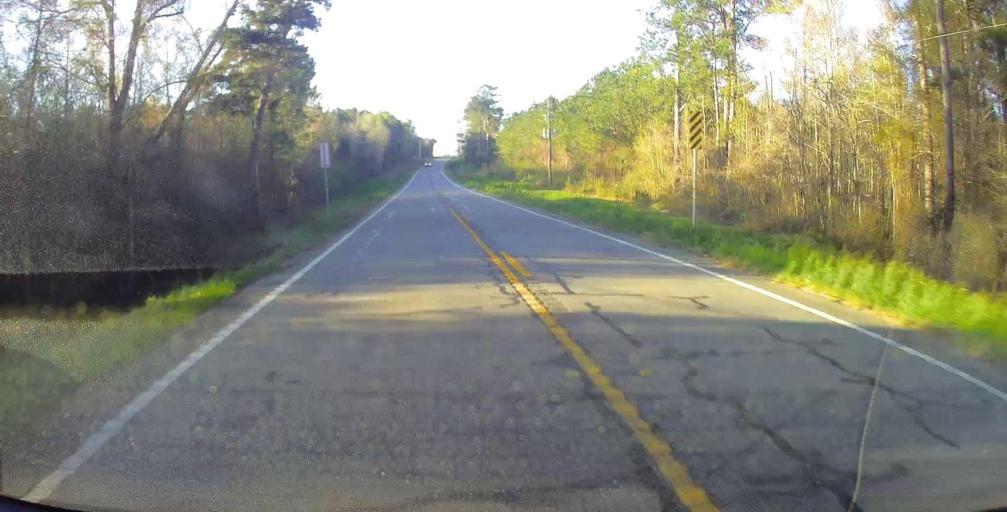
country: US
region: Georgia
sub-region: Wilcox County
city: Abbeville
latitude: 32.0278
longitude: -83.2501
